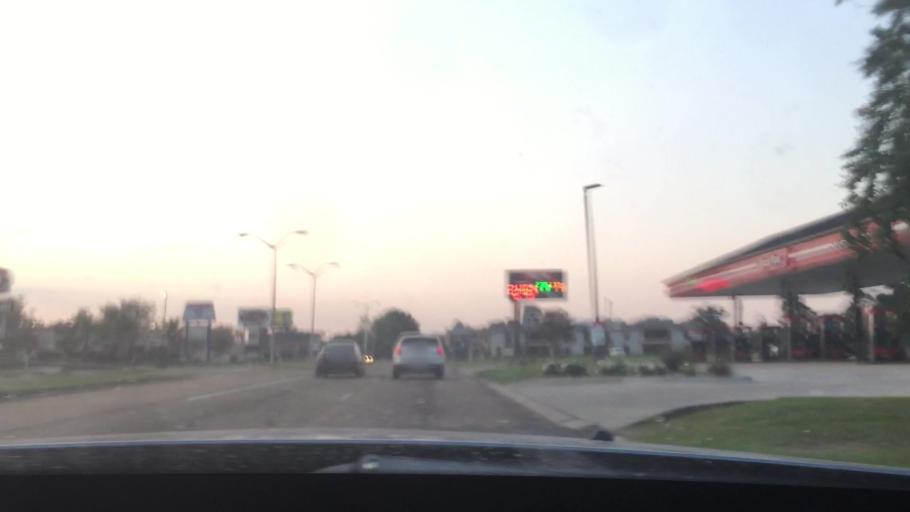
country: US
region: Louisiana
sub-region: East Baton Rouge Parish
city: Inniswold
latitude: 30.4214
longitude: -91.0515
